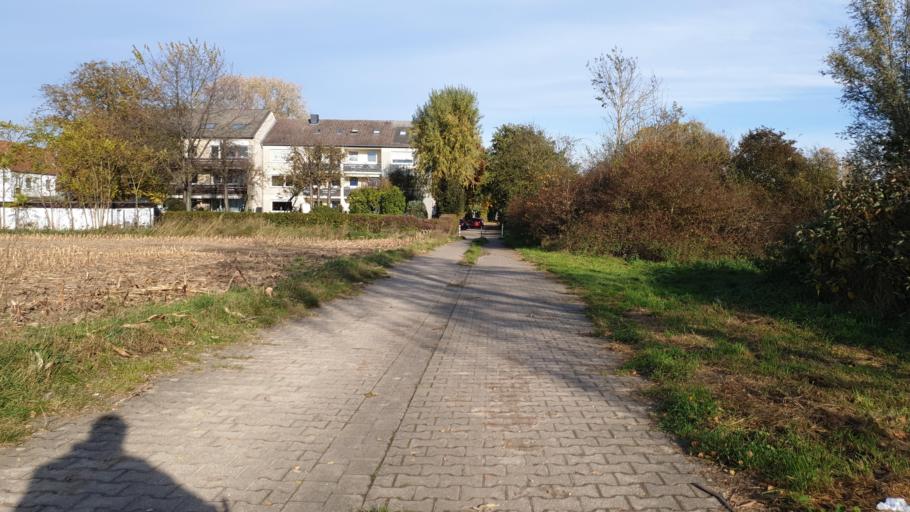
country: DE
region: North Rhine-Westphalia
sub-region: Regierungsbezirk Koln
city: Kerpen
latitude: 50.8966
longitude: 6.6699
